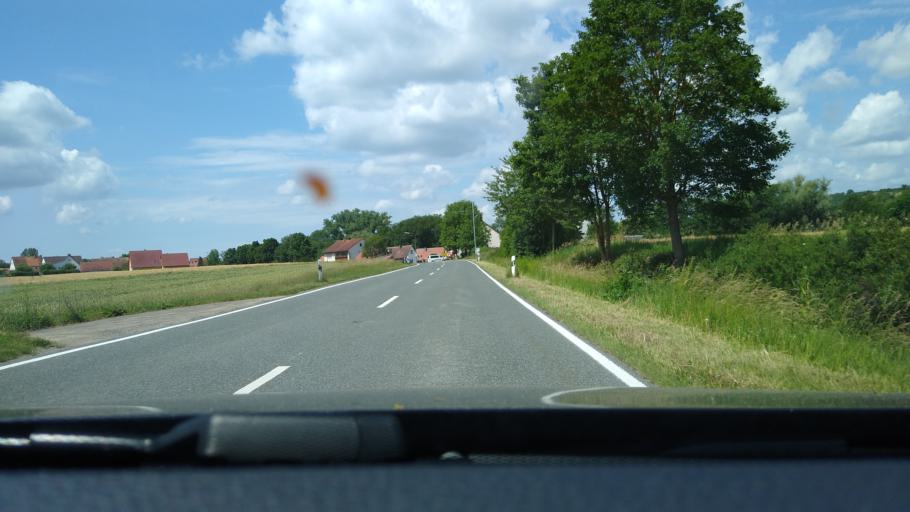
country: DE
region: Bavaria
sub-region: Regierungsbezirk Mittelfranken
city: Trautskirchen
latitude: 49.4596
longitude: 10.5435
